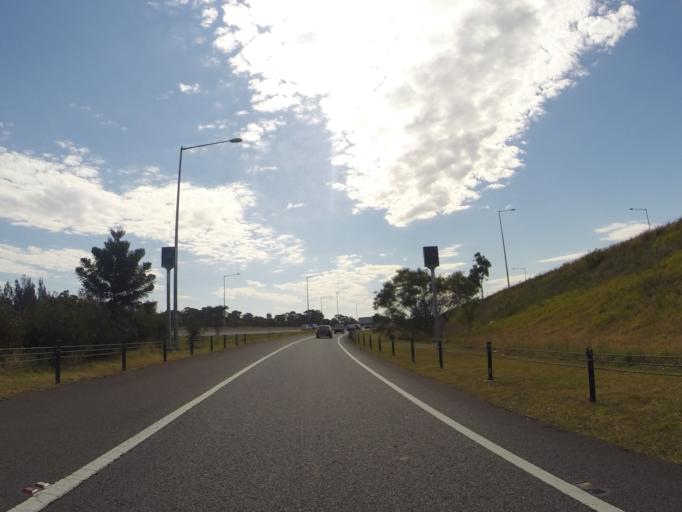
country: AU
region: New South Wales
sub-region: Liverpool
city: Miller
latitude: -33.9484
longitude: 150.8773
